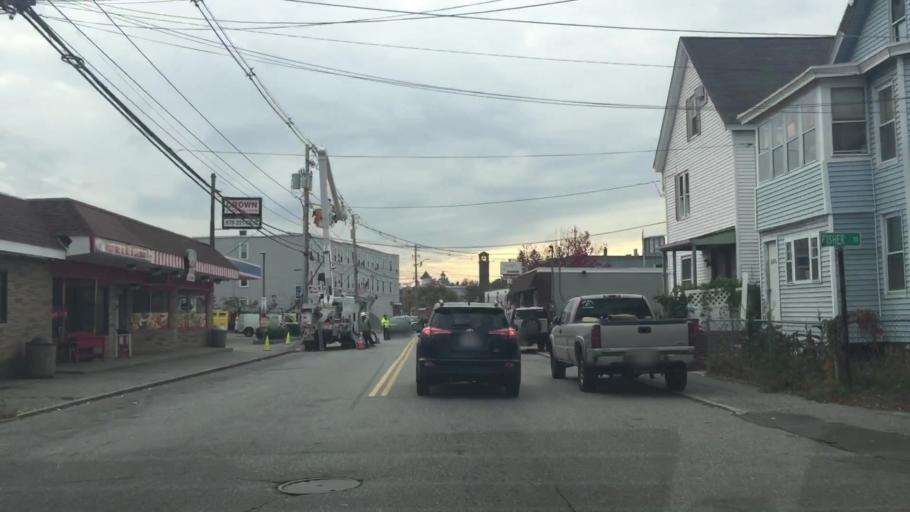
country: US
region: Massachusetts
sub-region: Middlesex County
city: Dracut
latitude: 42.6587
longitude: -71.3143
